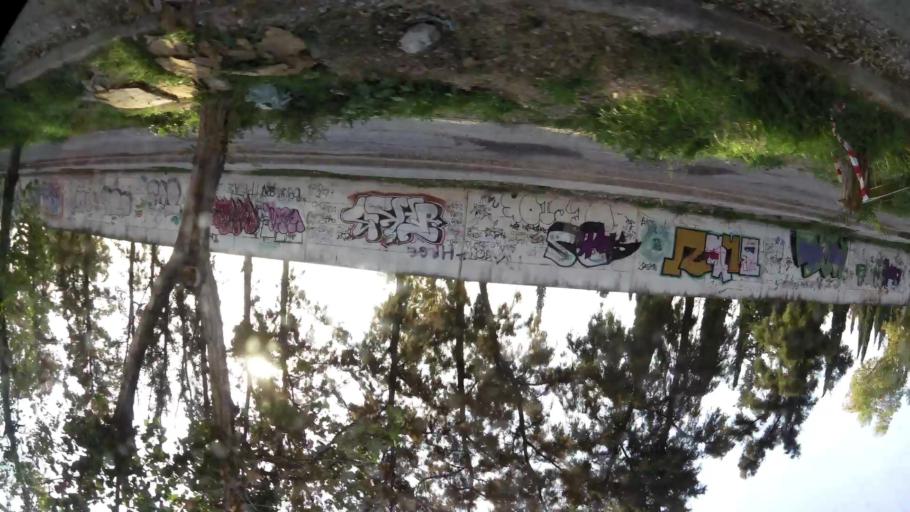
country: GR
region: Attica
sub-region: Nomarchia Athinas
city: Nea Filadelfeia
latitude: 38.0485
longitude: 23.7346
